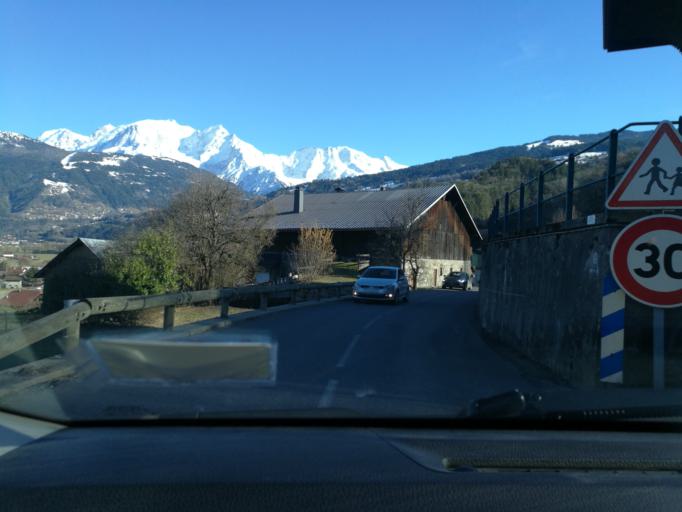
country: FR
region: Rhone-Alpes
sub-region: Departement de la Haute-Savoie
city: Domancy
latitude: 45.9131
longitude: 6.6488
